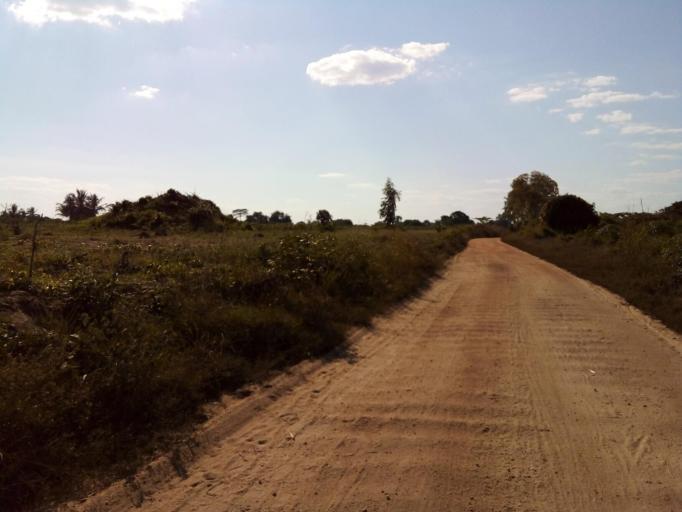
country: MZ
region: Zambezia
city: Quelimane
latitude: -17.5670
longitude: 36.6371
